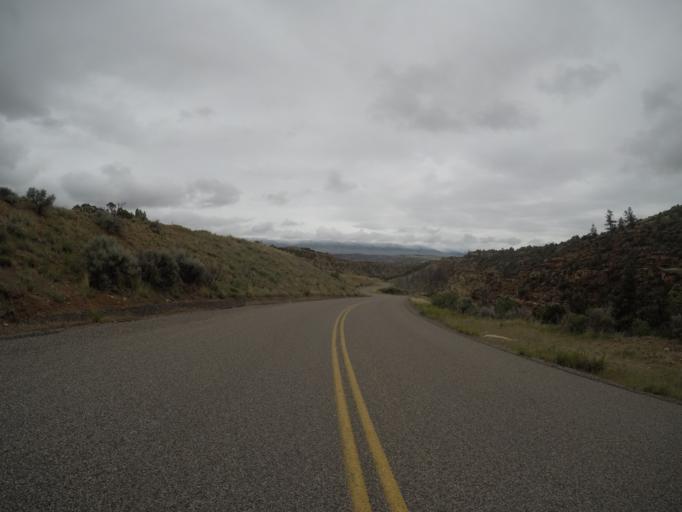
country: US
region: Wyoming
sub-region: Big Horn County
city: Lovell
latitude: 45.1090
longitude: -108.2396
